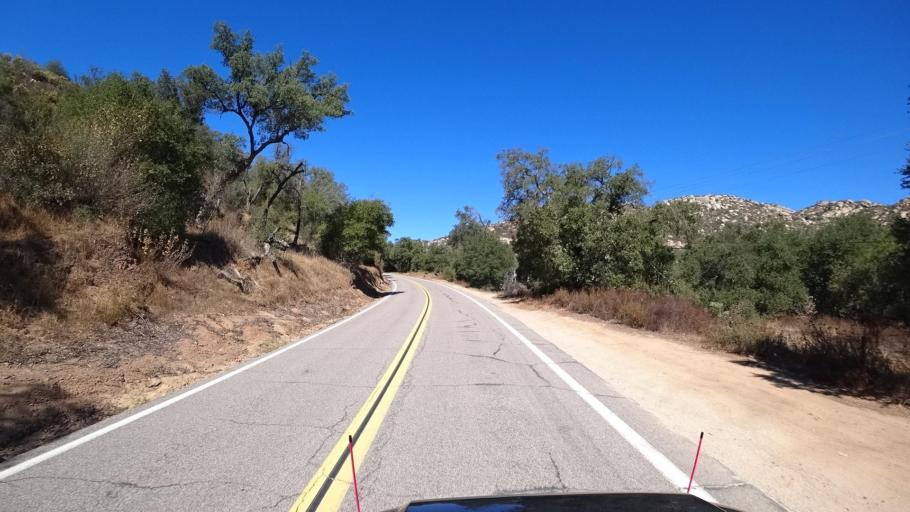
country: US
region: California
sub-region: San Diego County
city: Alpine
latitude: 32.7084
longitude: -116.7382
